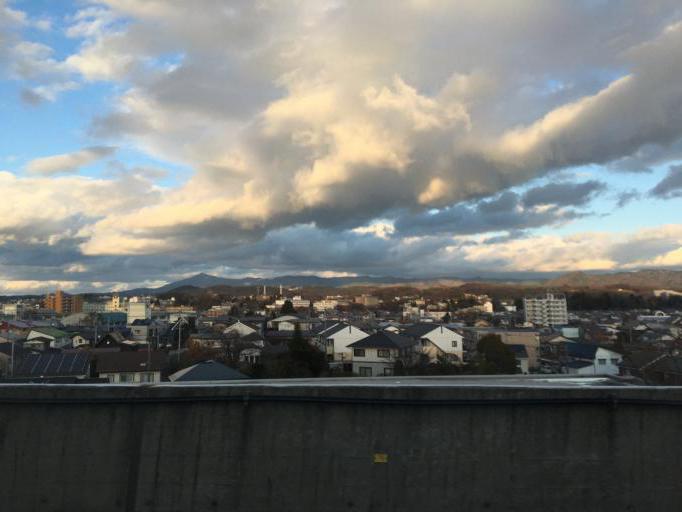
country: JP
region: Iwate
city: Morioka-shi
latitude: 39.7102
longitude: 141.1268
